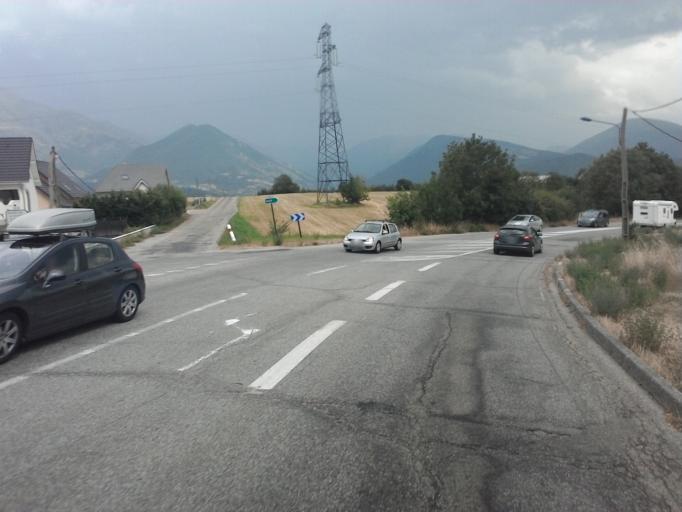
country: FR
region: Rhone-Alpes
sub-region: Departement de l'Isere
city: La Mure
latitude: 44.9052
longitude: 5.7969
